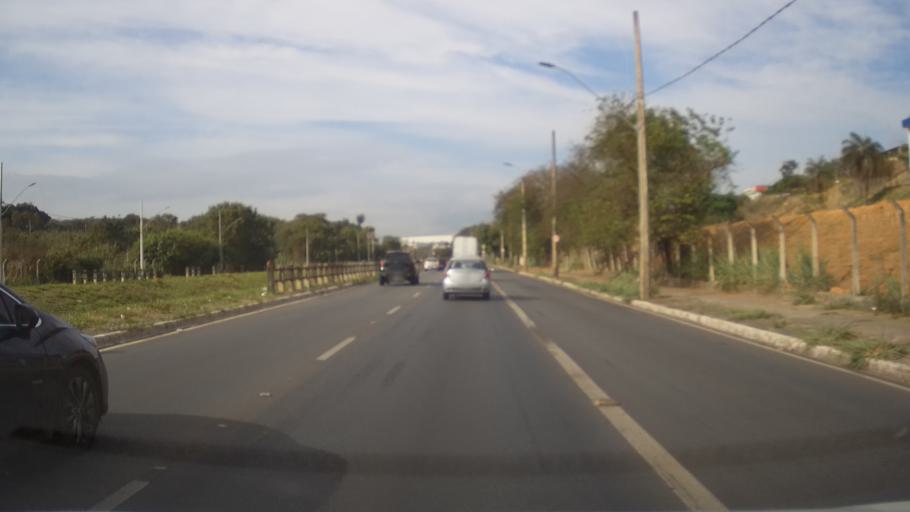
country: BR
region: Minas Gerais
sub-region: Contagem
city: Contagem
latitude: -19.8936
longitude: -44.0405
